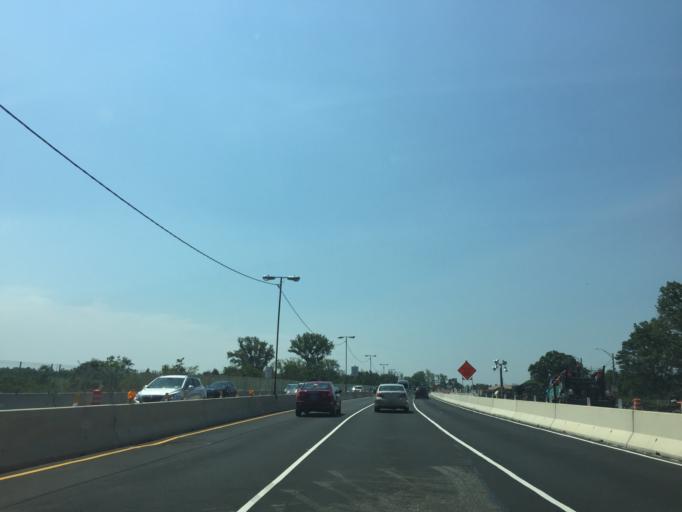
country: US
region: New York
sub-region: Kings County
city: East New York
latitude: 40.6156
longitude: -73.8970
